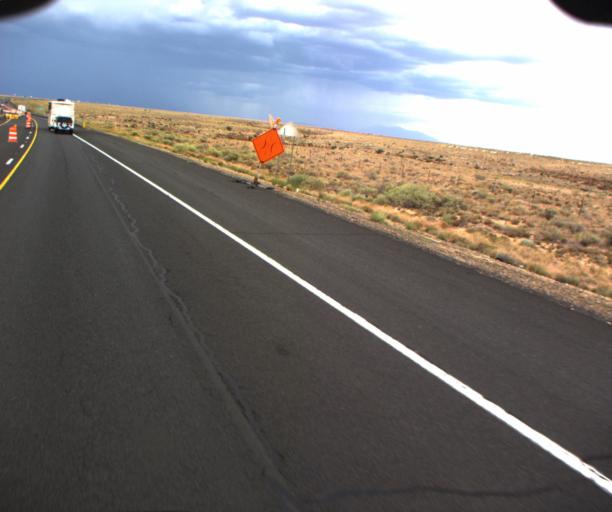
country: US
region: Arizona
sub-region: Coconino County
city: LeChee
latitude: 35.1181
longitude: -111.0968
